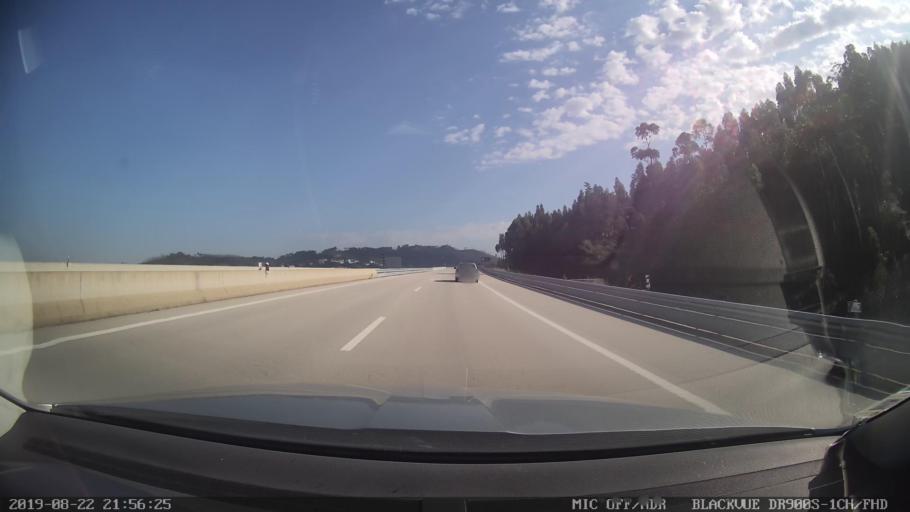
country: PT
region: Coimbra
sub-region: Coimbra
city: Coimbra
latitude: 40.1700
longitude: -8.3782
